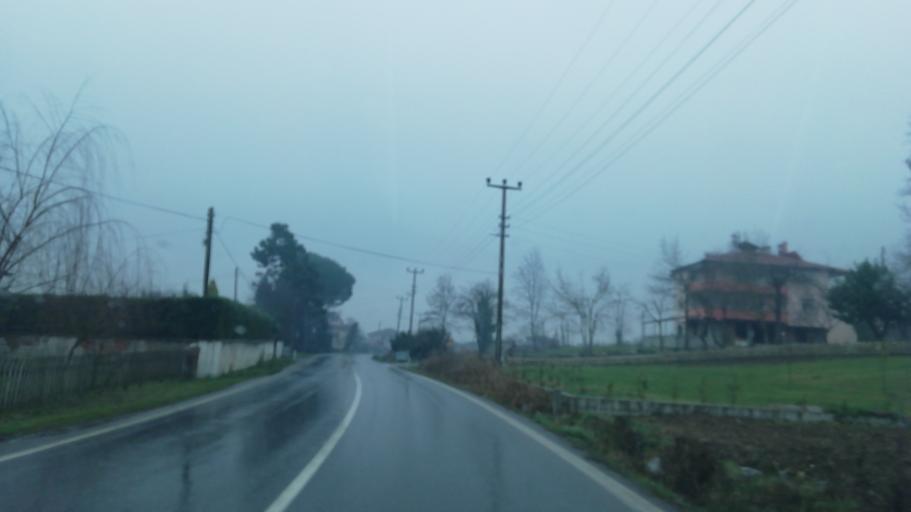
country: TR
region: Sakarya
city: Karapurcek
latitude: 40.6889
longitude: 30.4805
